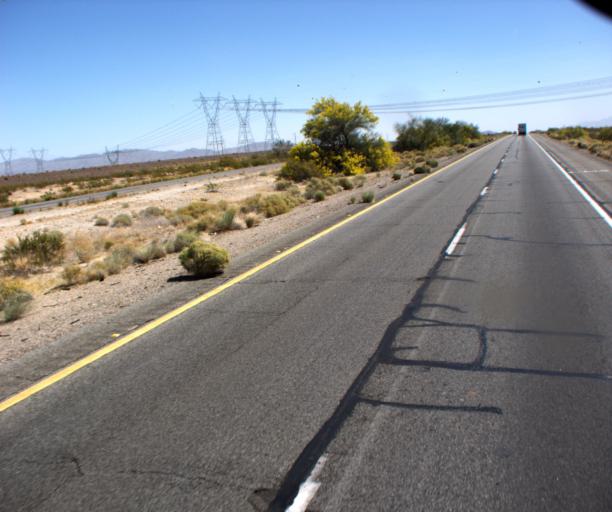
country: US
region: Arizona
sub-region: Maricopa County
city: Buckeye
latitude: 33.4535
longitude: -112.7416
